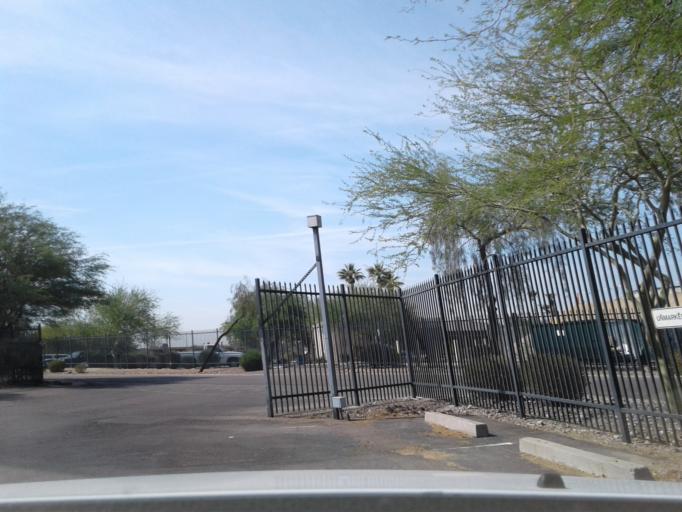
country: US
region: Arizona
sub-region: Maricopa County
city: Paradise Valley
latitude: 33.5280
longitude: -112.0312
